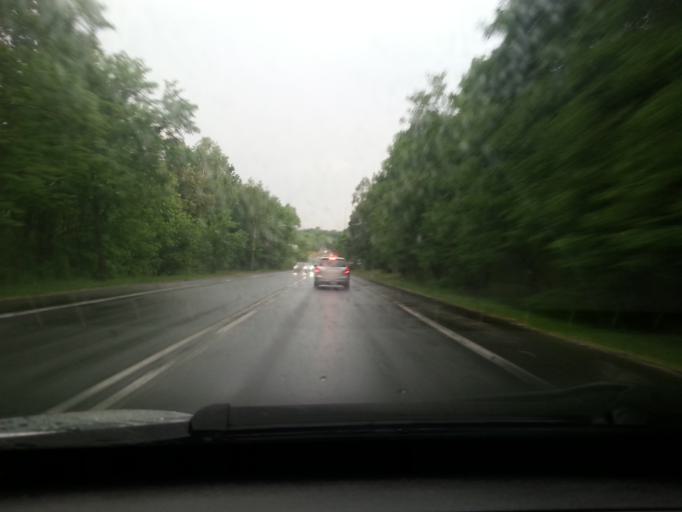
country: PL
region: Lodz Voivodeship
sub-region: Powiat zgierski
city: Strykow
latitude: 51.8462
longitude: 19.5600
